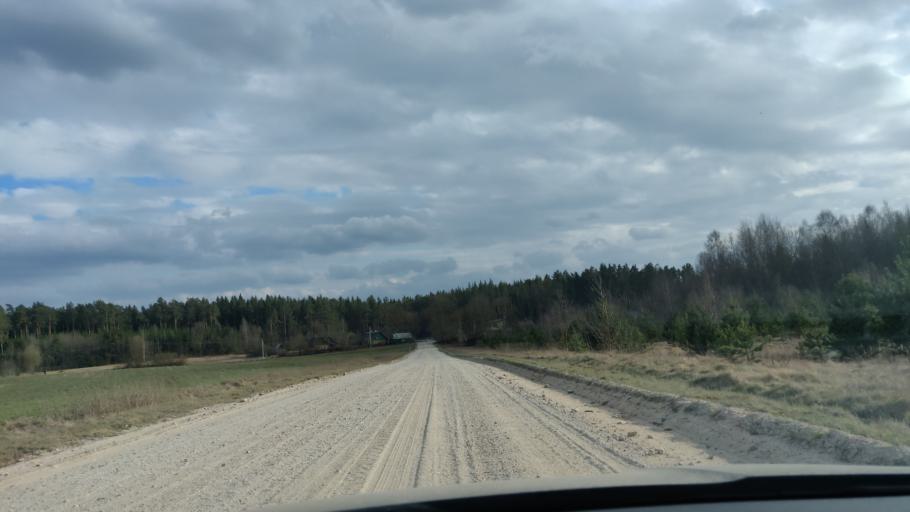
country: LT
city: Lentvaris
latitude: 54.6053
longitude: 25.0749
